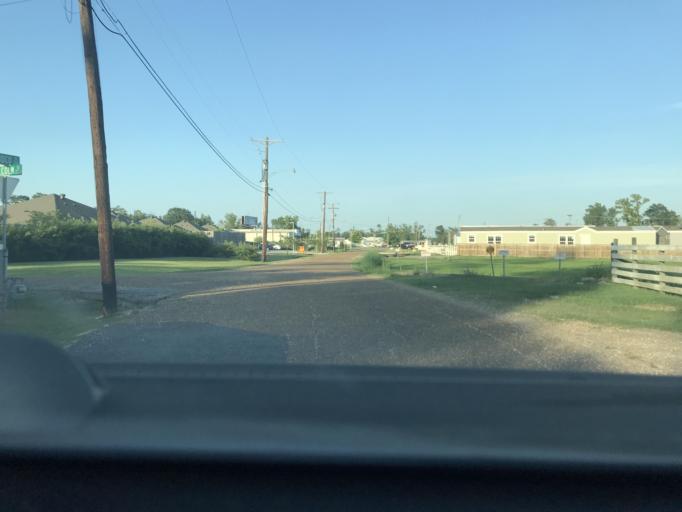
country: US
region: Louisiana
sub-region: Calcasieu Parish
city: Moss Bluff
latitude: 30.2652
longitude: -93.1829
